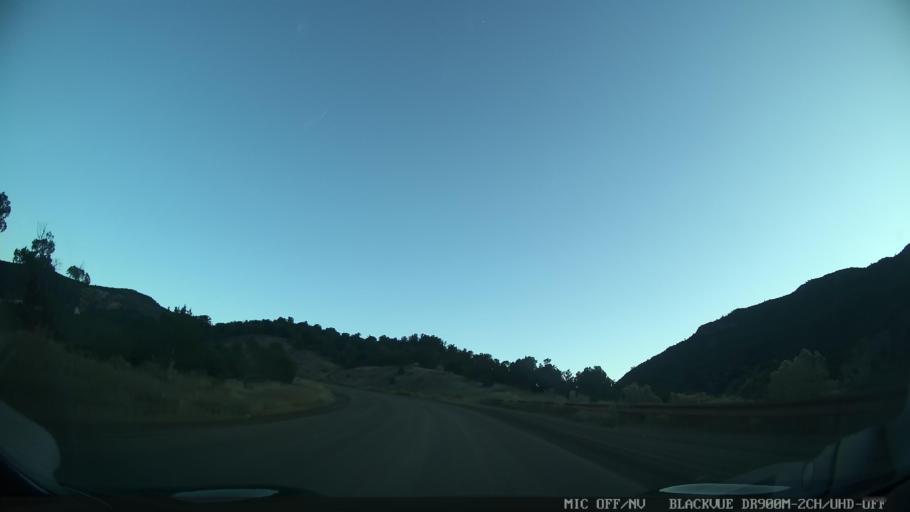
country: US
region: Colorado
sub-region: Eagle County
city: Edwards
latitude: 39.8564
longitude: -106.6432
